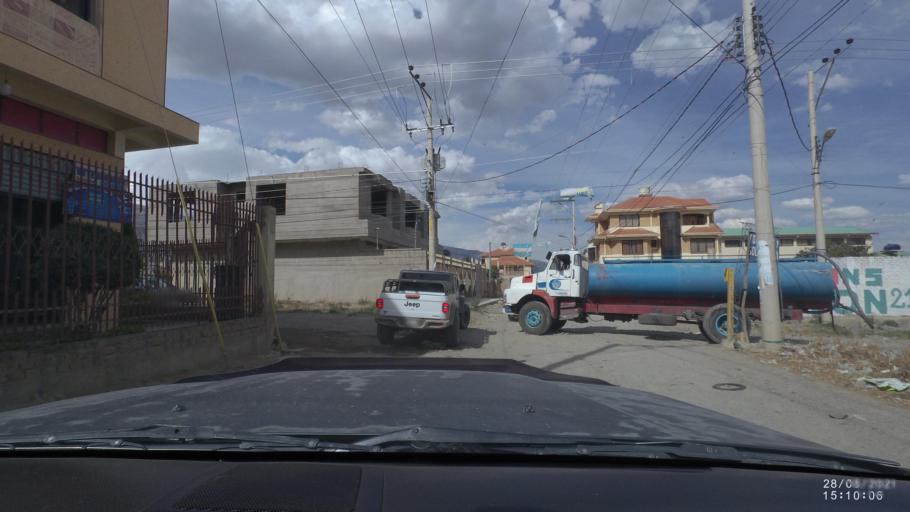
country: BO
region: Cochabamba
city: Cochabamba
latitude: -17.3385
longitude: -66.2689
